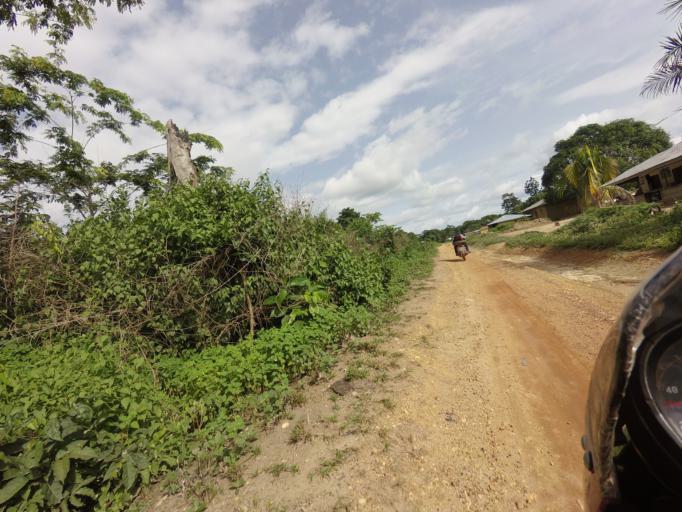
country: SL
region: Eastern Province
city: Jojoima
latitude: 7.8139
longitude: -10.8151
